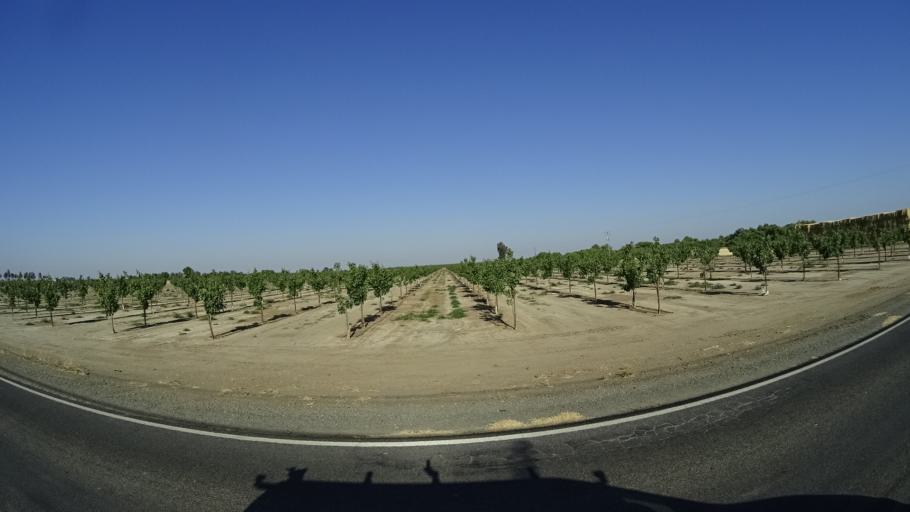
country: US
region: California
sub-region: Kings County
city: Armona
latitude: 36.2743
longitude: -119.7091
